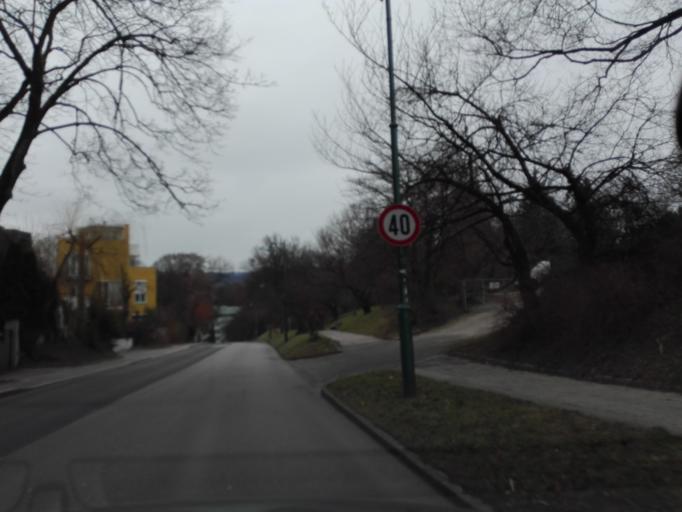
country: AT
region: Upper Austria
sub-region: Linz Stadt
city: Linz
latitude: 48.2956
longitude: 14.2749
